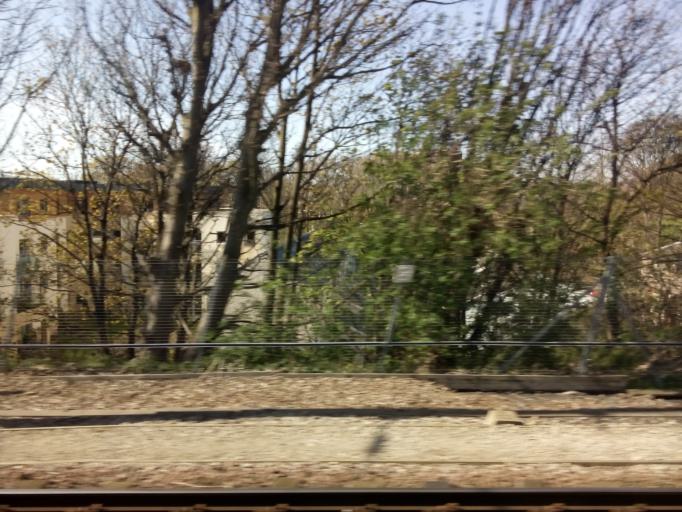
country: GB
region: Scotland
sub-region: West Lothian
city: Seafield
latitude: 55.9505
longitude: -3.1196
